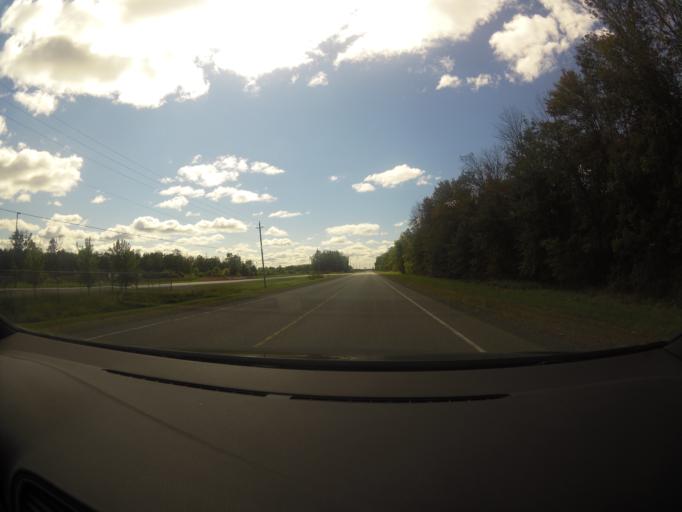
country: CA
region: Ontario
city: Carleton Place
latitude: 45.1668
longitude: -76.0644
